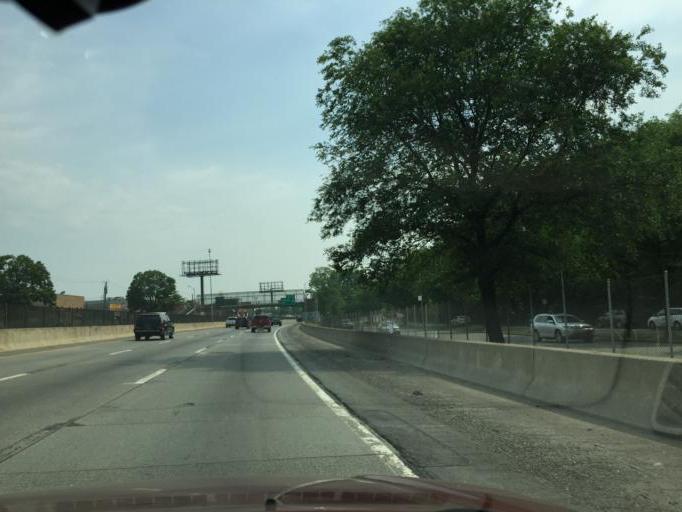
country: US
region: New York
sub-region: Bronx
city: Eastchester
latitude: 40.8807
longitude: -73.8313
